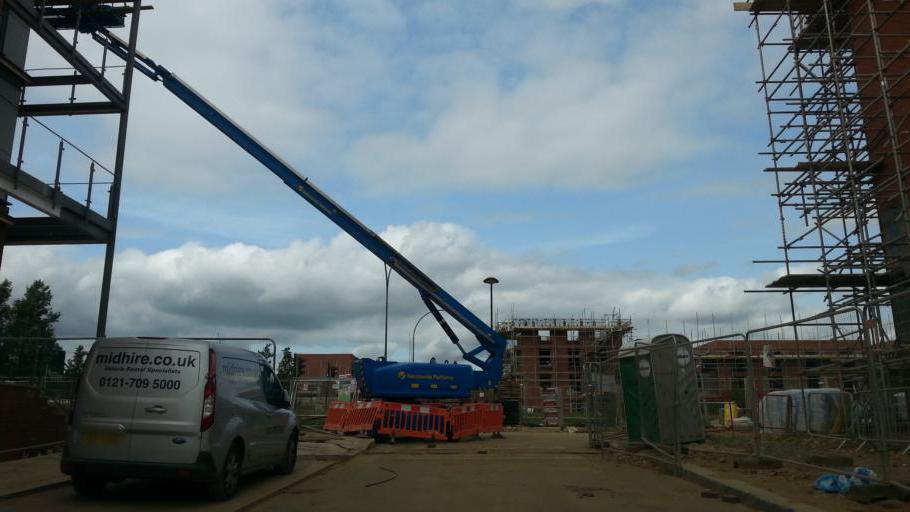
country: GB
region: England
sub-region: Northamptonshire
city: Blisworth
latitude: 52.2363
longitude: -0.9436
